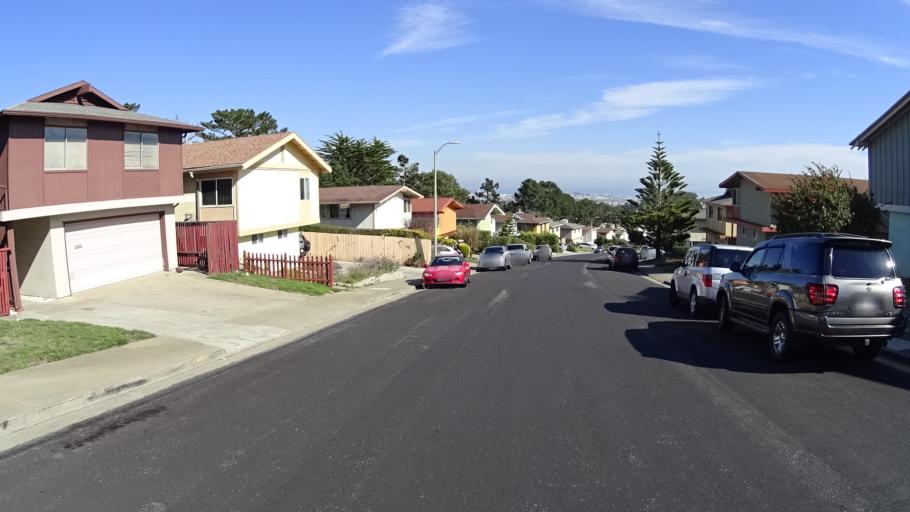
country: US
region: California
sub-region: San Mateo County
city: Colma
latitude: 37.6429
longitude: -122.4598
